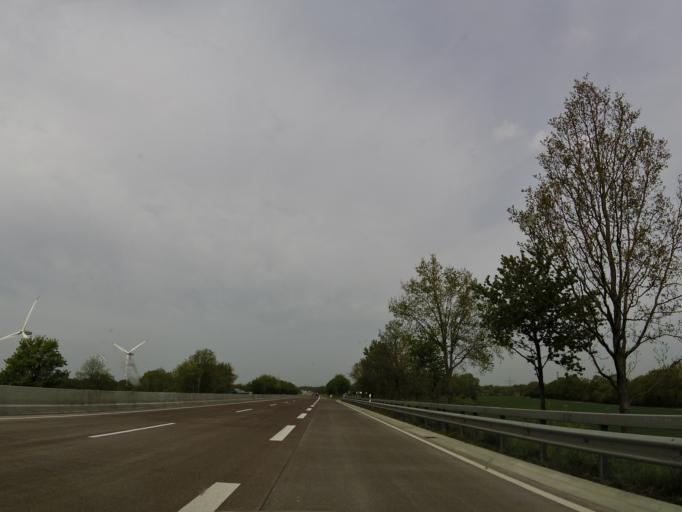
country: DE
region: Schleswig-Holstein
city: Horst
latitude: 53.8267
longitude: 9.6374
